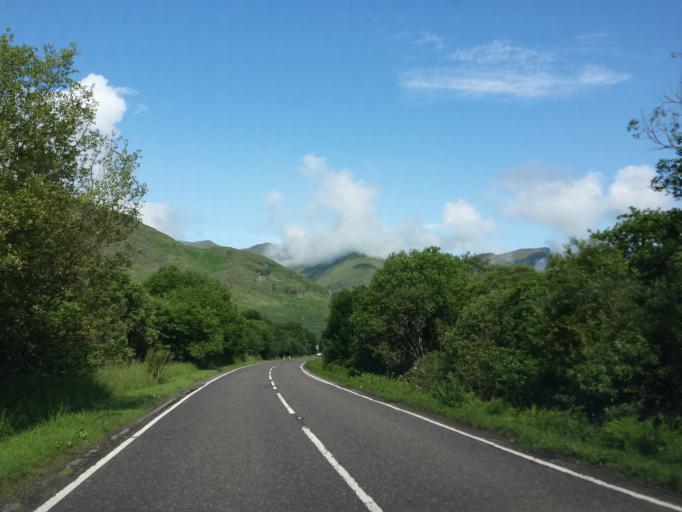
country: GB
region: Scotland
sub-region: Argyll and Bute
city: Garelochhead
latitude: 56.4064
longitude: -5.0150
